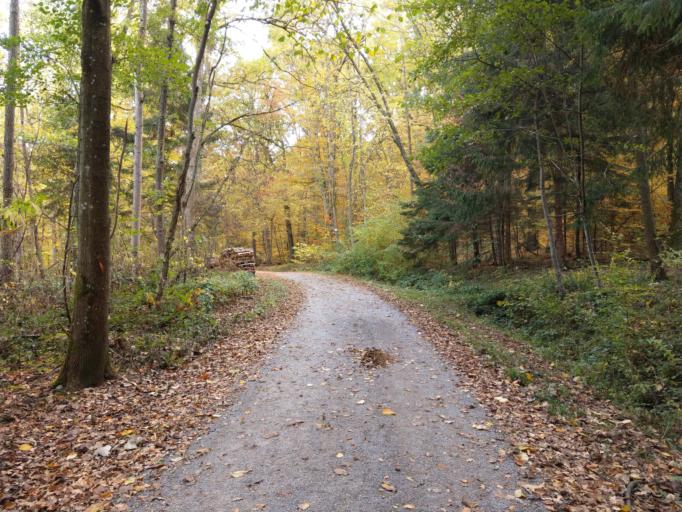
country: DE
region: Baden-Wuerttemberg
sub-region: Regierungsbezirk Stuttgart
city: Filderstadt
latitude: 48.6397
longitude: 9.2064
